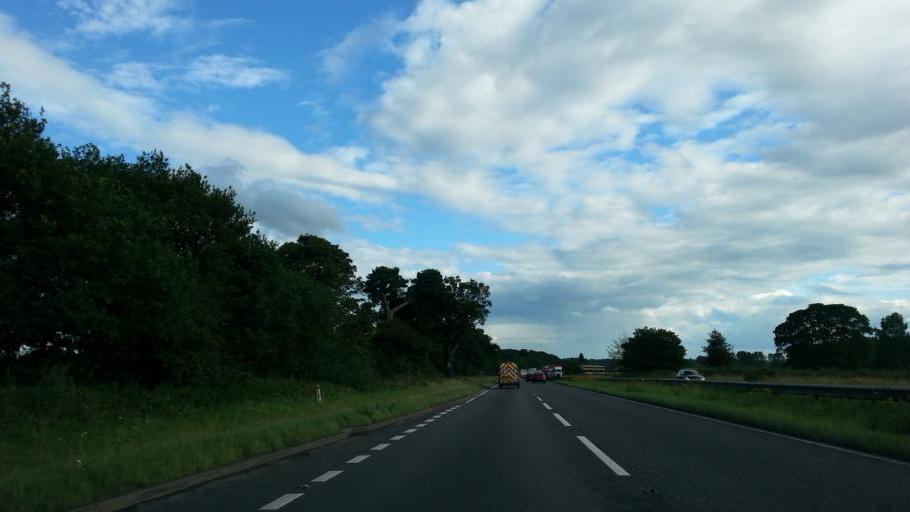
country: GB
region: England
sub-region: Nottinghamshire
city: Babworth
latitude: 53.3440
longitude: -1.0304
